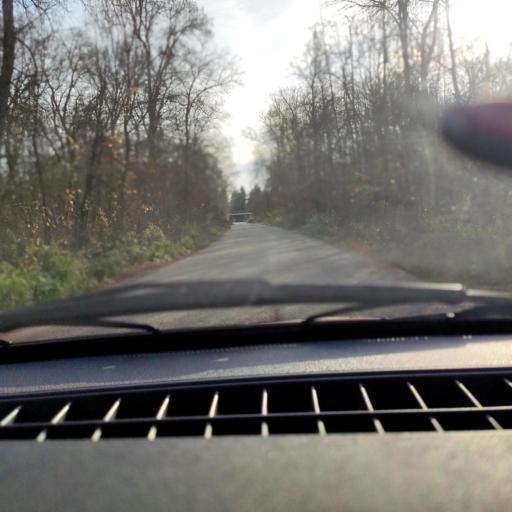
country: RU
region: Bashkortostan
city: Ufa
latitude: 54.7827
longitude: 56.1744
